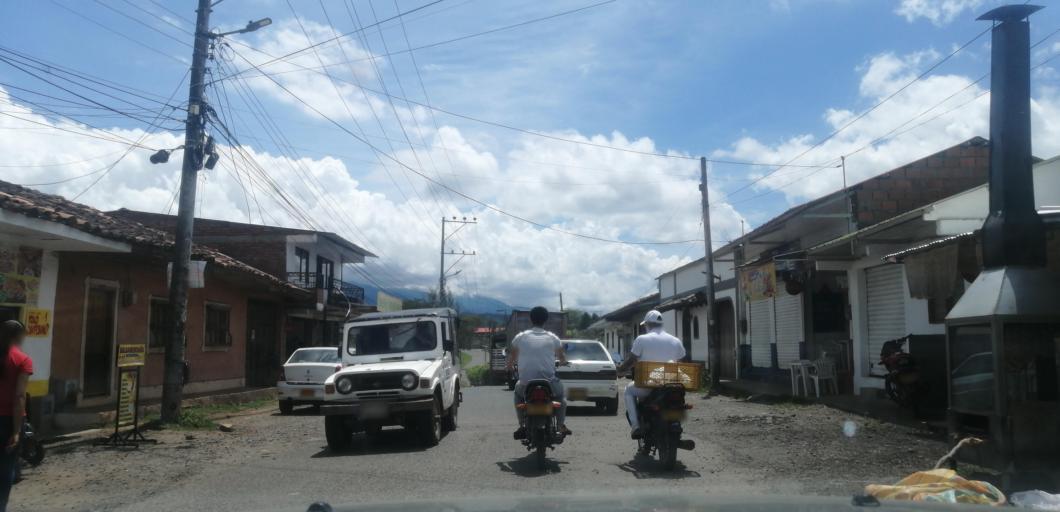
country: CO
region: Valle del Cauca
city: Restrepo
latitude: 3.8256
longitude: -76.5212
